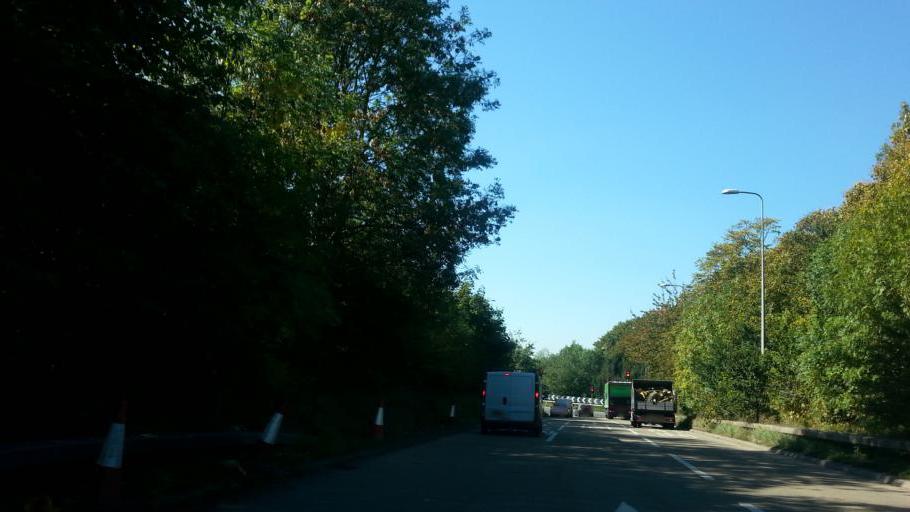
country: GB
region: England
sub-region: Derbyshire
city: Long Eaton
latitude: 52.9166
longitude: -1.2962
